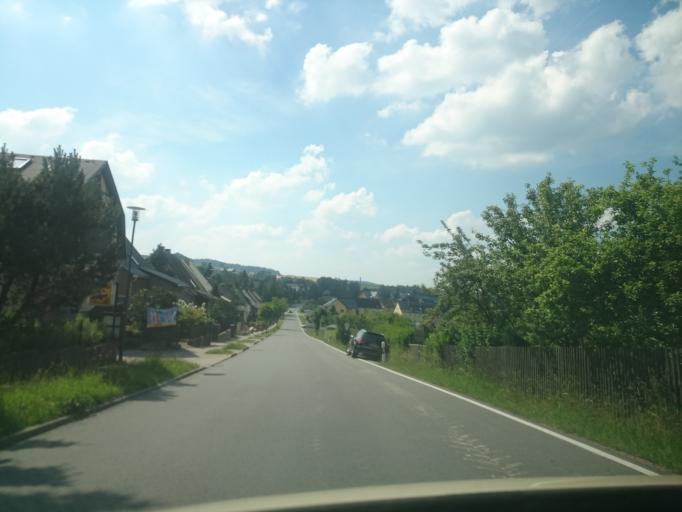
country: DE
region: Saxony
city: Lengefeld
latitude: 50.7146
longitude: 13.2015
